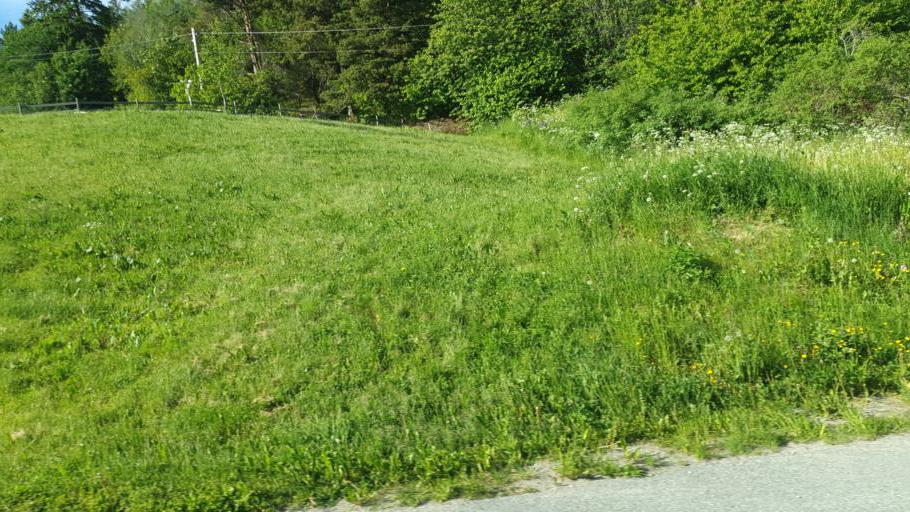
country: NO
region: Sor-Trondelag
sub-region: Rissa
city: Rissa
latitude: 63.4971
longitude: 10.0968
